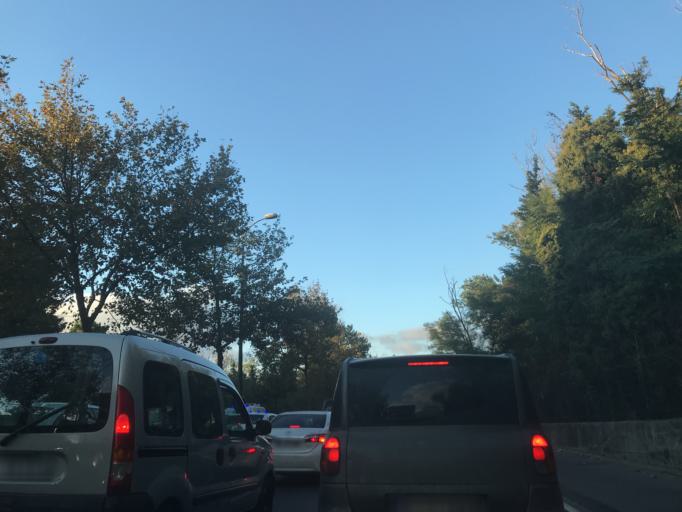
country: TR
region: Istanbul
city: Sisli
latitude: 41.1259
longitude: 29.0238
